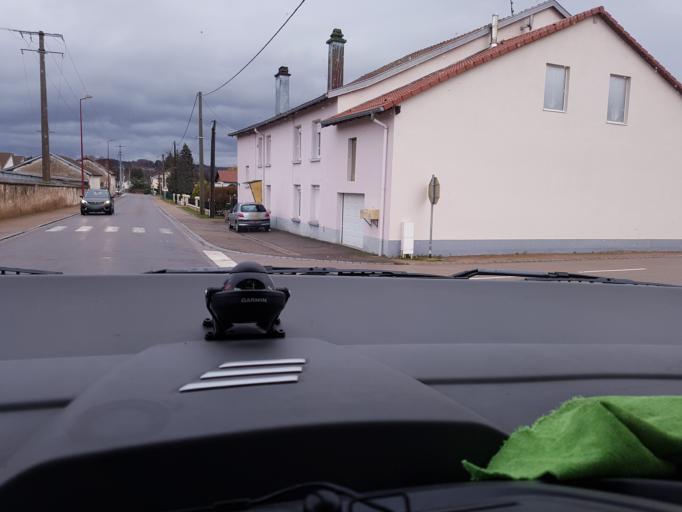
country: FR
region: Lorraine
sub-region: Departement des Vosges
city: Saint-Michel-sur-Meurthe
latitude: 48.3213
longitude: 6.8908
